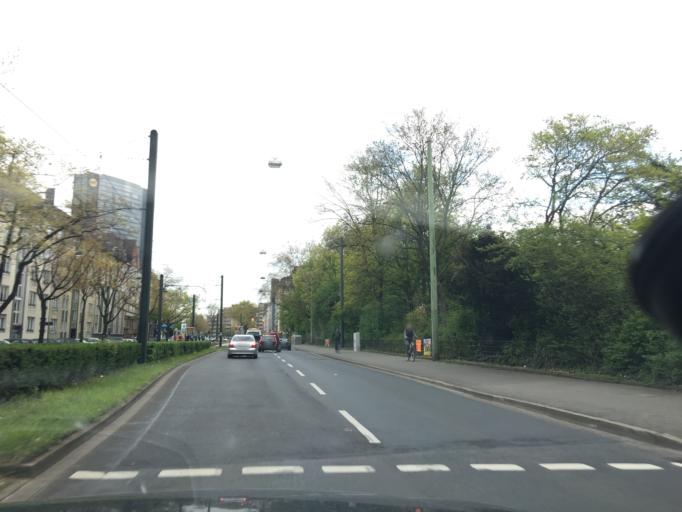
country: DE
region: North Rhine-Westphalia
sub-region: Regierungsbezirk Dusseldorf
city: Dusseldorf
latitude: 51.2457
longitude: 6.8019
